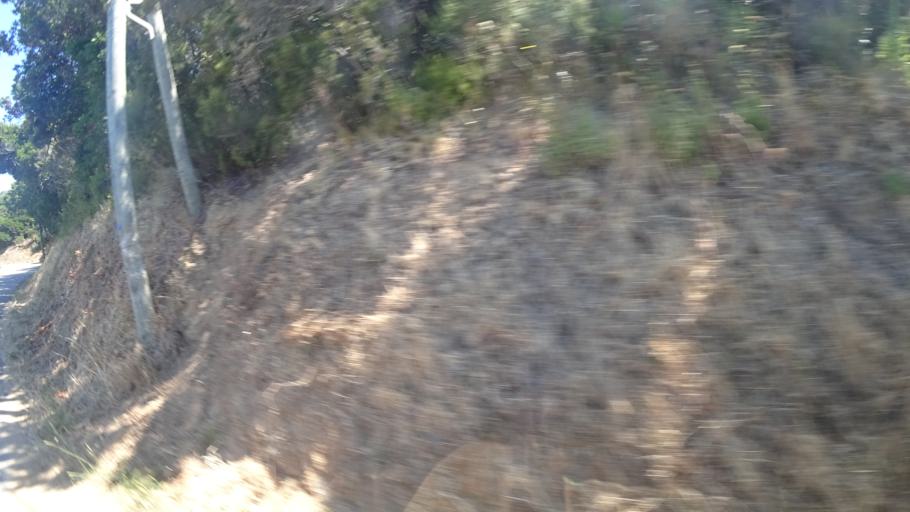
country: FR
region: Corsica
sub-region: Departement de la Corse-du-Sud
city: Alata
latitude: 41.9800
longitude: 8.6729
